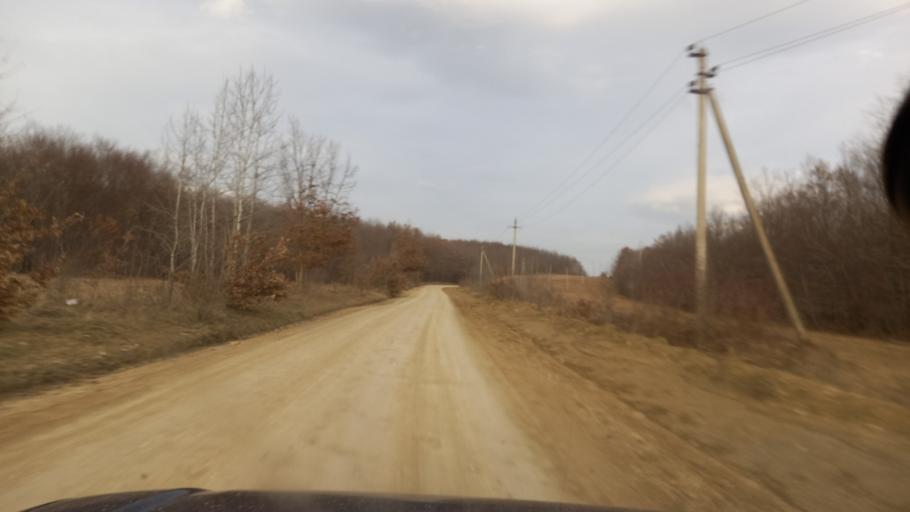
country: RU
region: Adygeya
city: Kamennomostskiy
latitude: 44.1735
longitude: 40.2482
